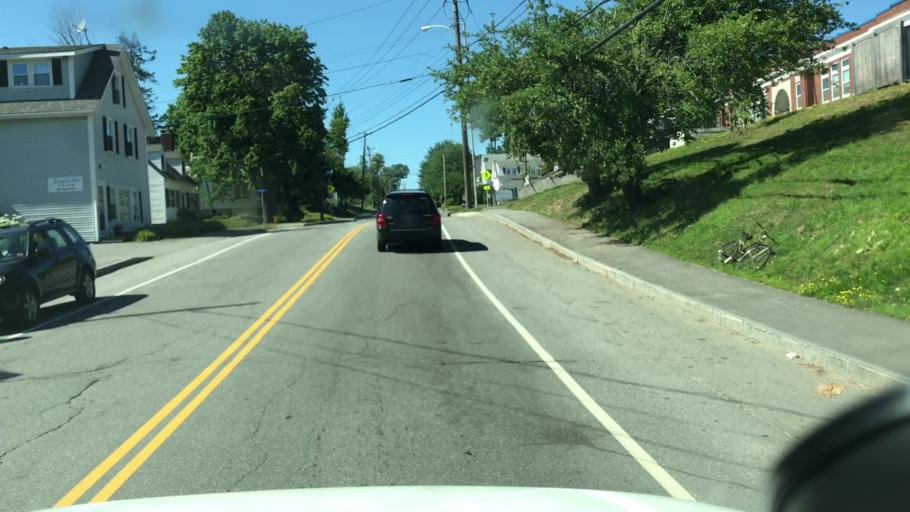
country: US
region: Maine
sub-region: Hancock County
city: Ellsworth
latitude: 44.5457
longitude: -68.4257
